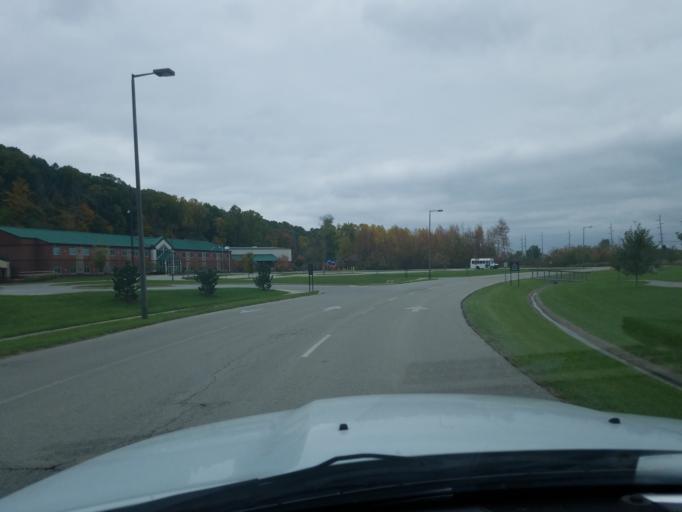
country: US
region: Kentucky
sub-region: Jefferson County
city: Pleasure Ridge Park
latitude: 38.1426
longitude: -85.8361
